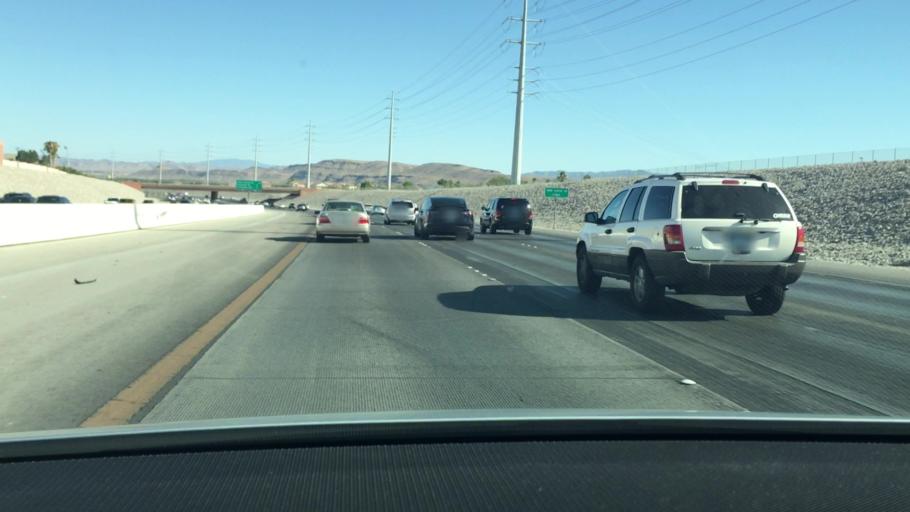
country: US
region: Nevada
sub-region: Clark County
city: Summerlin South
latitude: 36.1330
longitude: -115.3361
